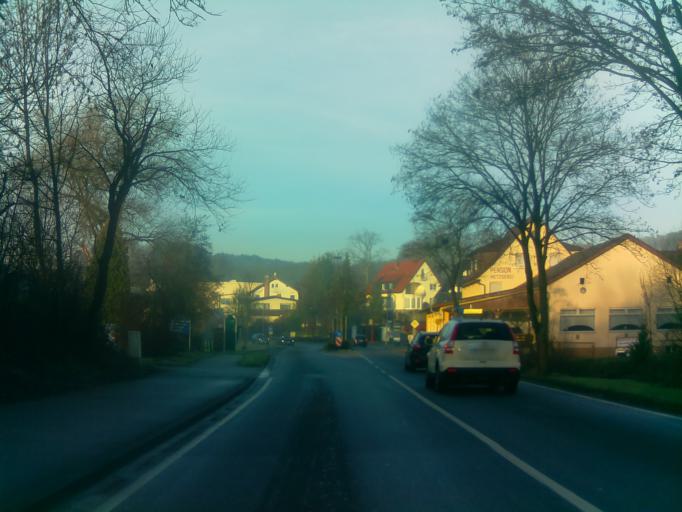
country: DE
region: Hesse
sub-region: Regierungsbezirk Darmstadt
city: Rimbach
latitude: 49.6473
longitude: 8.7439
